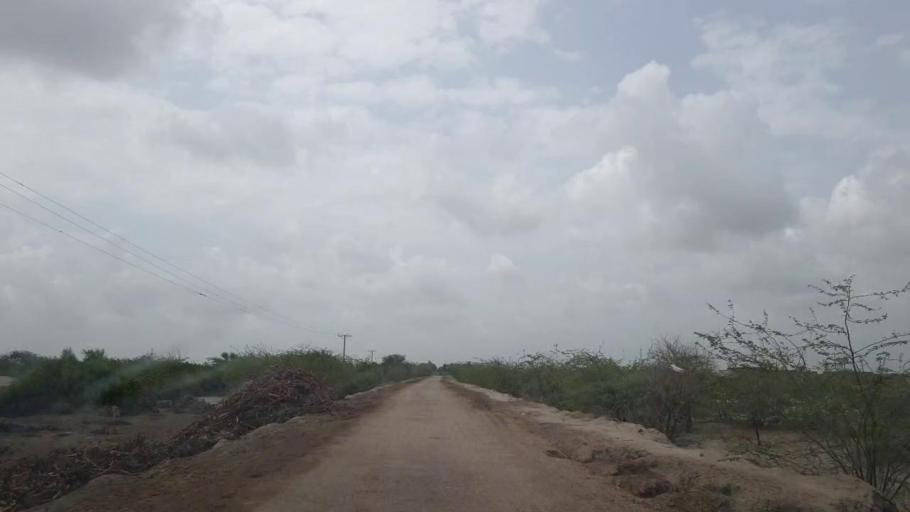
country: PK
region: Sindh
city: Naukot
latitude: 24.9463
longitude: 69.2586
